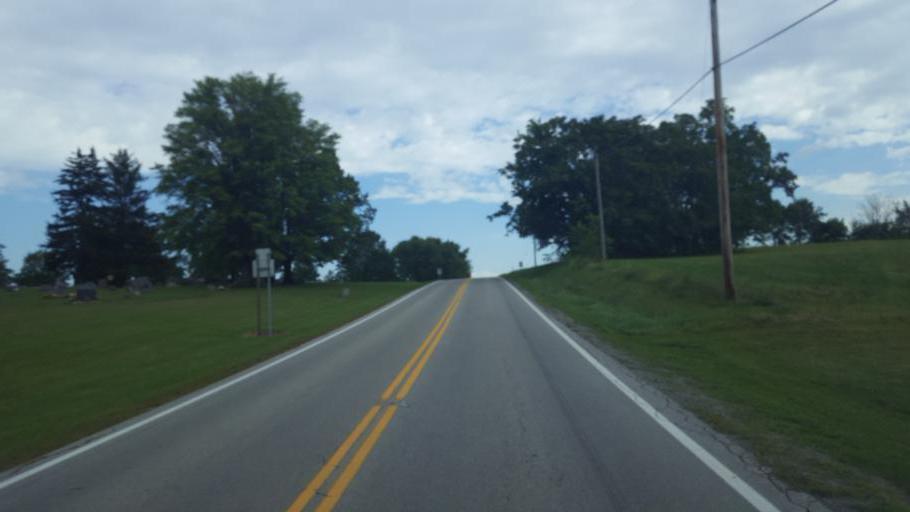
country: US
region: Ohio
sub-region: Seneca County
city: Tiffin
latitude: 40.9597
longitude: -83.1680
